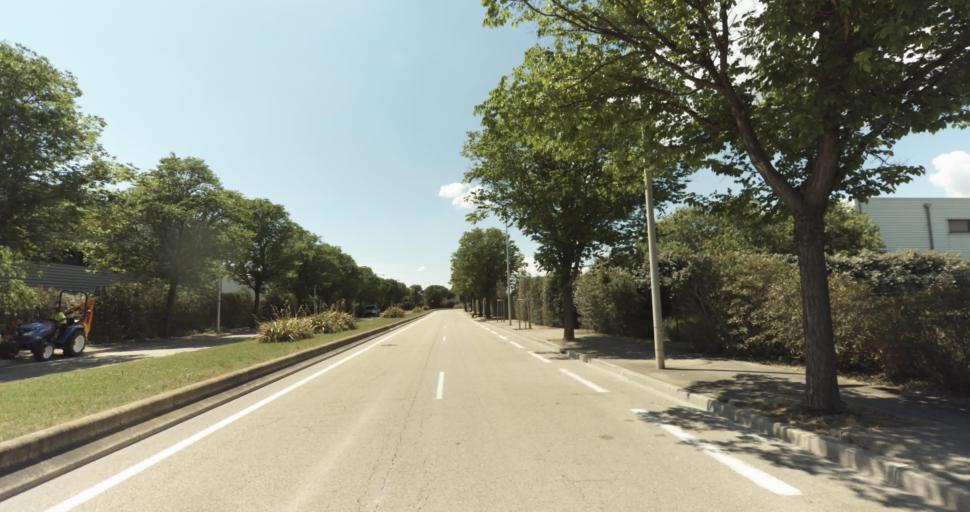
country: FR
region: Languedoc-Roussillon
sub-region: Departement du Gard
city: Nimes
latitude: 43.8102
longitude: 4.3361
